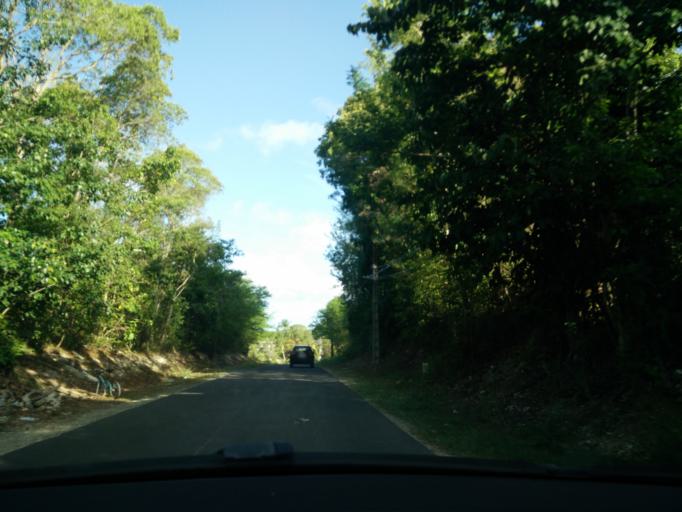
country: GP
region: Guadeloupe
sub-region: Guadeloupe
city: Sainte-Anne
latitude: 16.2772
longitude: -61.3988
